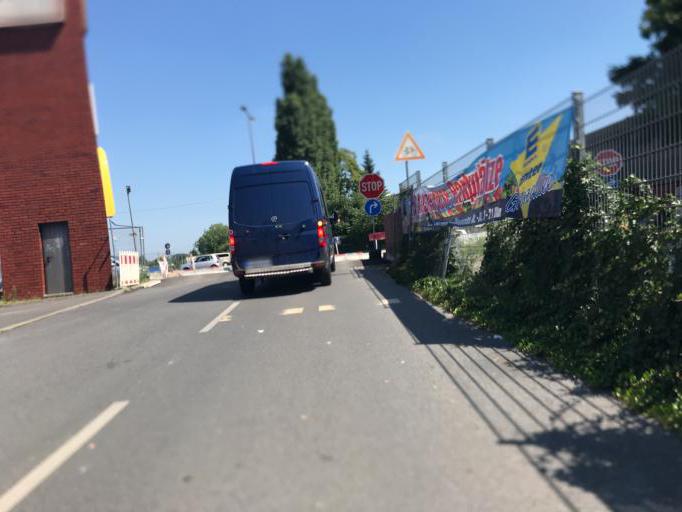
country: DE
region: Berlin
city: Plaenterwald
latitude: 52.4708
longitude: 13.4617
